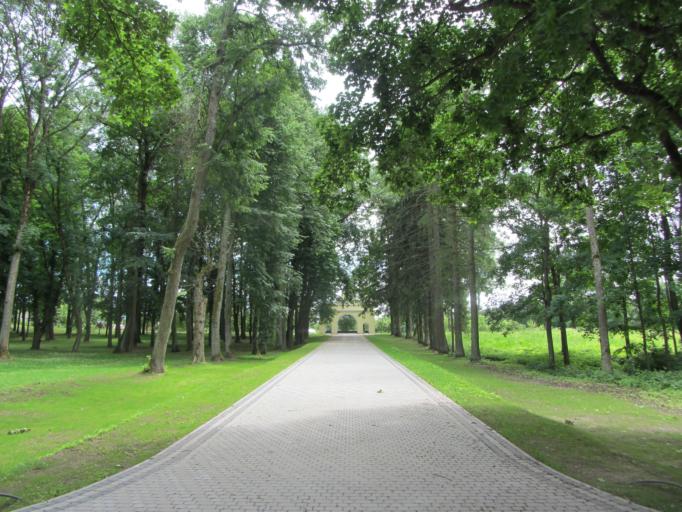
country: LT
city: Sirvintos
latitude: 54.9398
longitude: 24.9364
